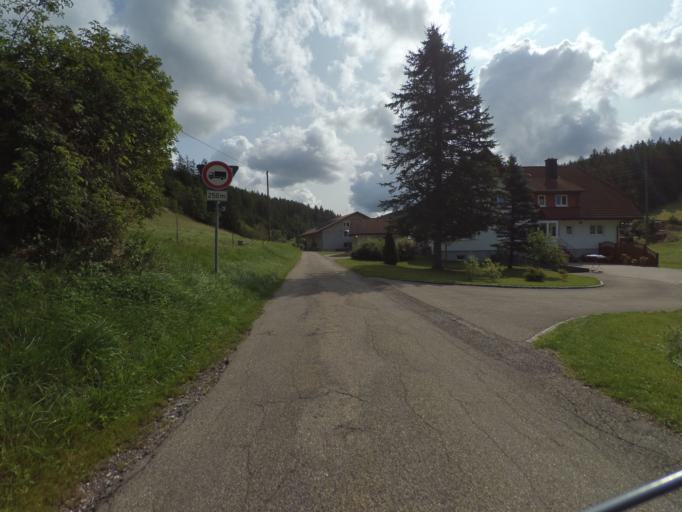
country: DE
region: Baden-Wuerttemberg
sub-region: Freiburg Region
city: Eisenbach
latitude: 47.9772
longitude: 8.2826
